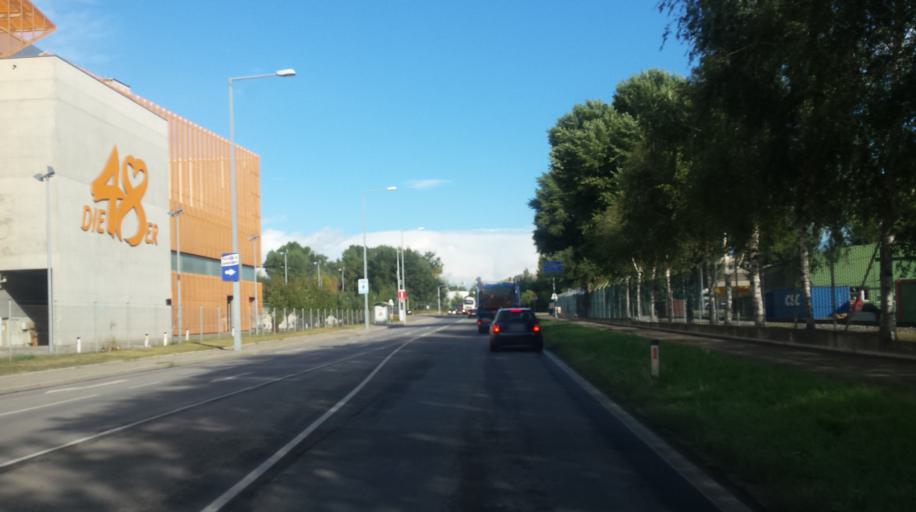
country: AT
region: Lower Austria
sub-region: Politischer Bezirk Wien-Umgebung
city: Schwechat
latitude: 48.1757
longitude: 16.4613
